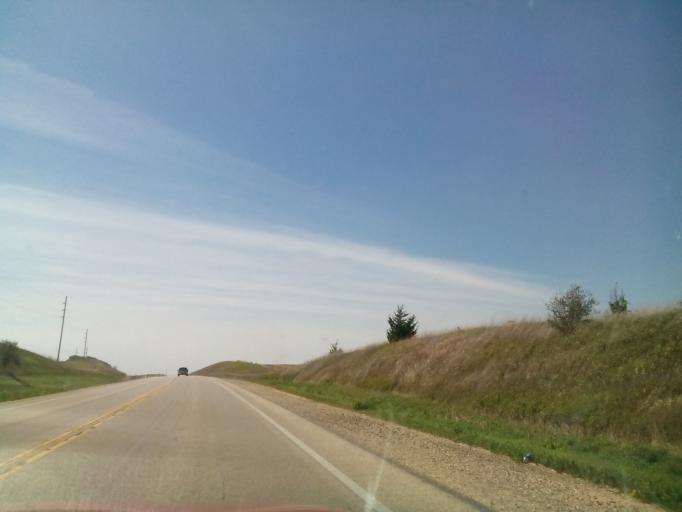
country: US
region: Wisconsin
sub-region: Green County
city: Monroe
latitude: 42.6539
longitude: -89.6301
